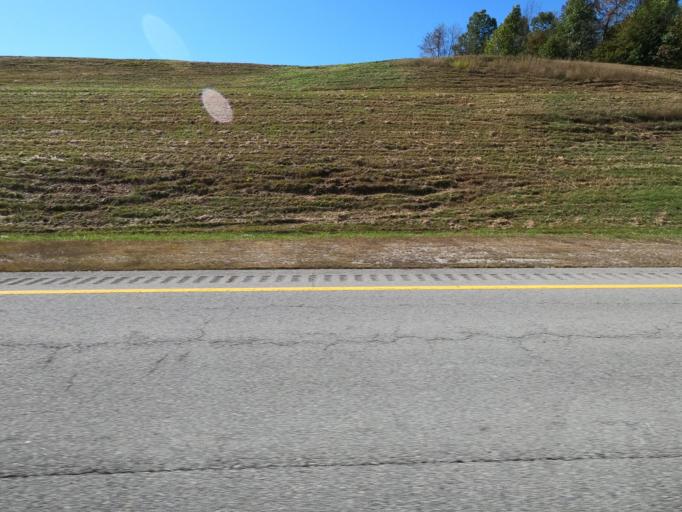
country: US
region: Tennessee
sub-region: Williamson County
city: Fairview
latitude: 35.8902
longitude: -87.1171
